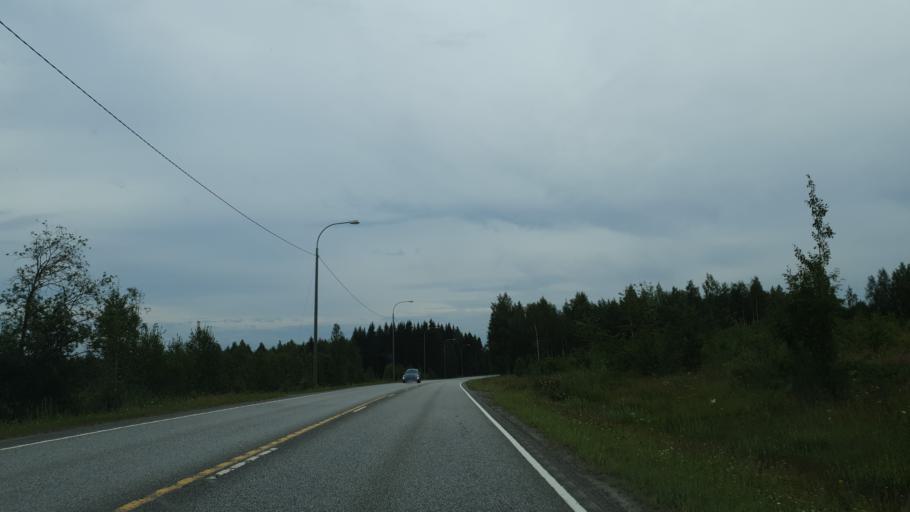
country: FI
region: North Karelia
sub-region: Joensuu
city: Pyhaeselkae
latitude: 62.4617
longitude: 30.0024
